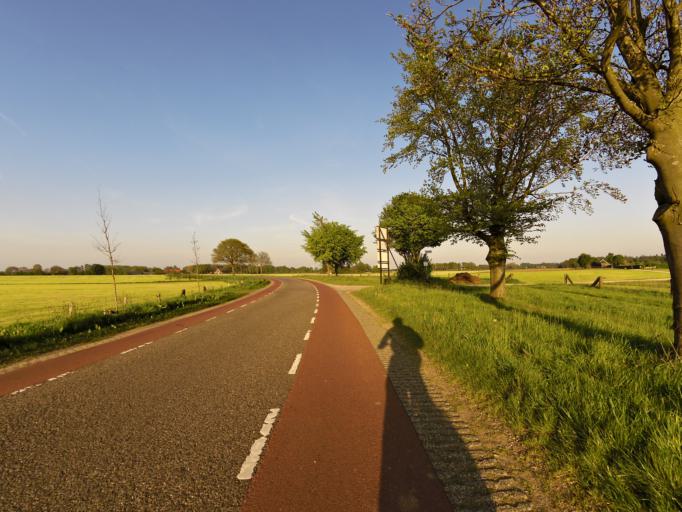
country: NL
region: Gelderland
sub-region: Oude IJsselstreek
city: Gendringen
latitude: 51.8766
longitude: 6.4016
